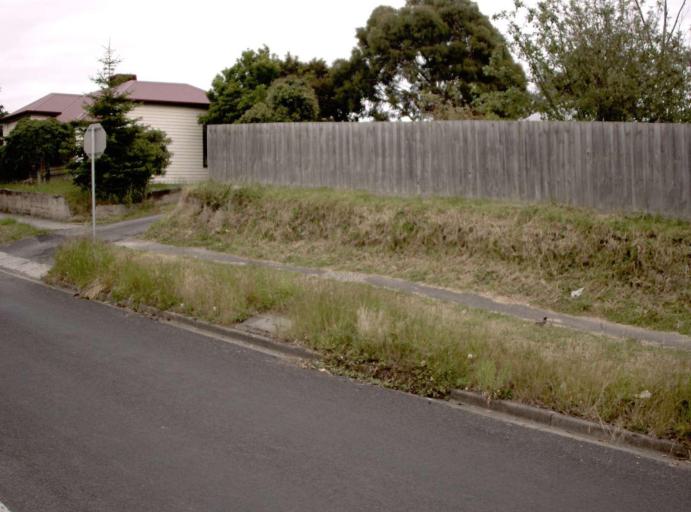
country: AU
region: Victoria
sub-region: Bass Coast
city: North Wonthaggi
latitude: -38.4362
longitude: 145.8160
